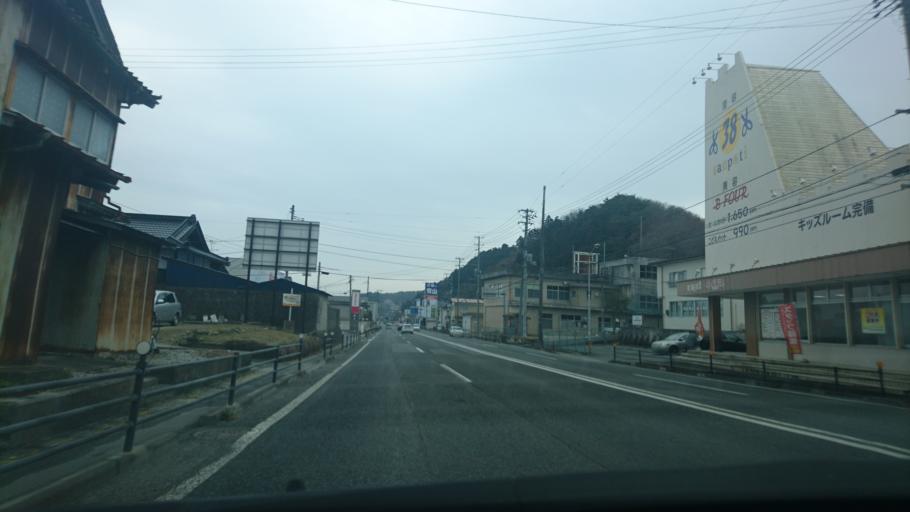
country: JP
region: Iwate
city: Ofunato
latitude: 39.0906
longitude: 141.7064
